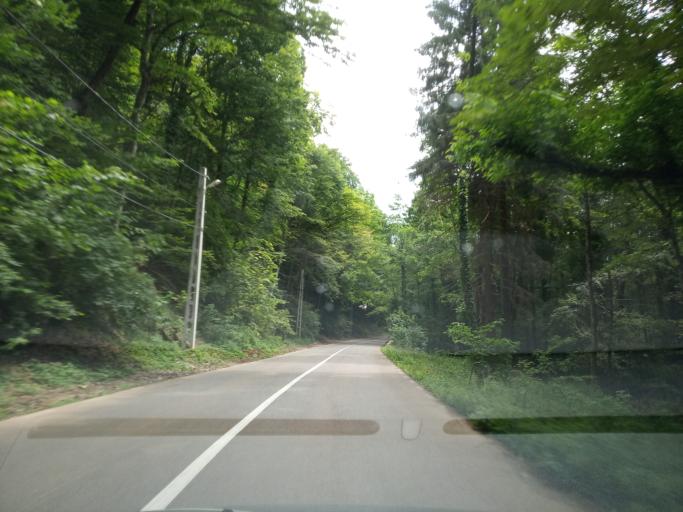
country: RO
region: Gorj
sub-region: Comuna Tismana
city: Pocruia
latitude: 45.0812
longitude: 22.9280
